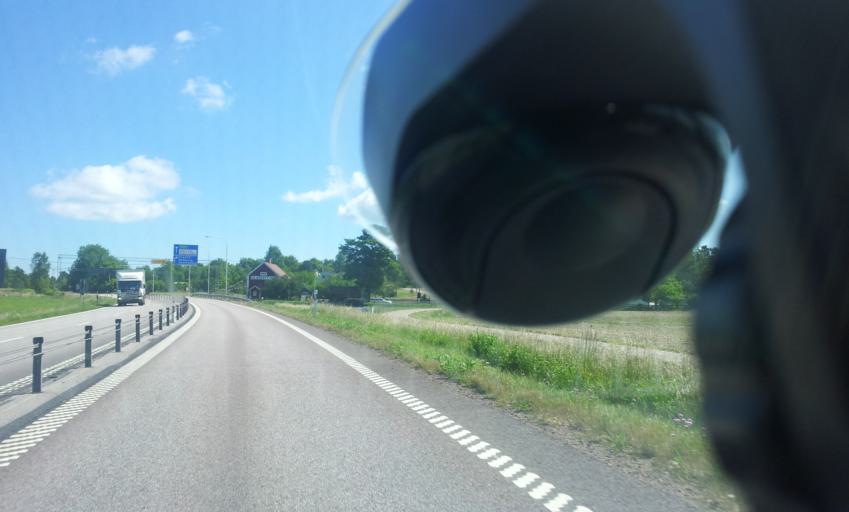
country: SE
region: Kalmar
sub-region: Monsteras Kommun
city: Moensteras
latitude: 57.0666
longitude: 16.4660
